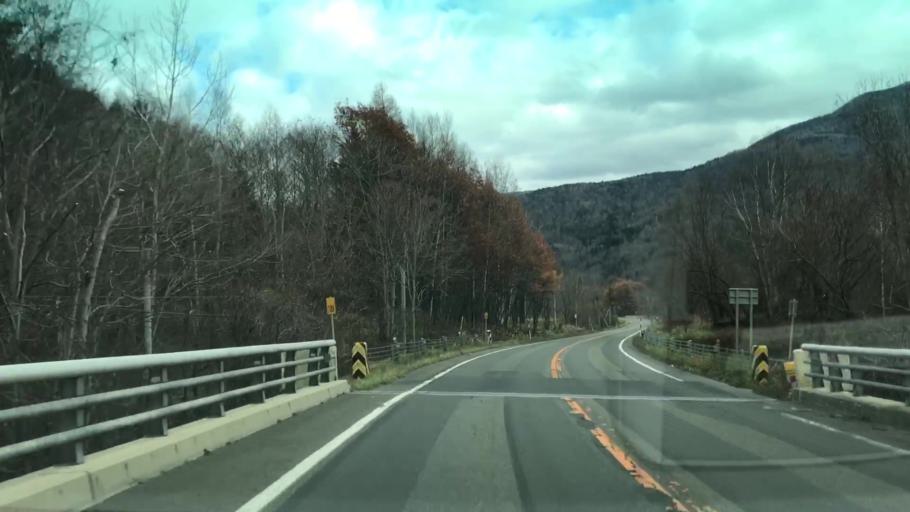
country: JP
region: Hokkaido
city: Shizunai-furukawacho
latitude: 42.8122
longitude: 142.4091
